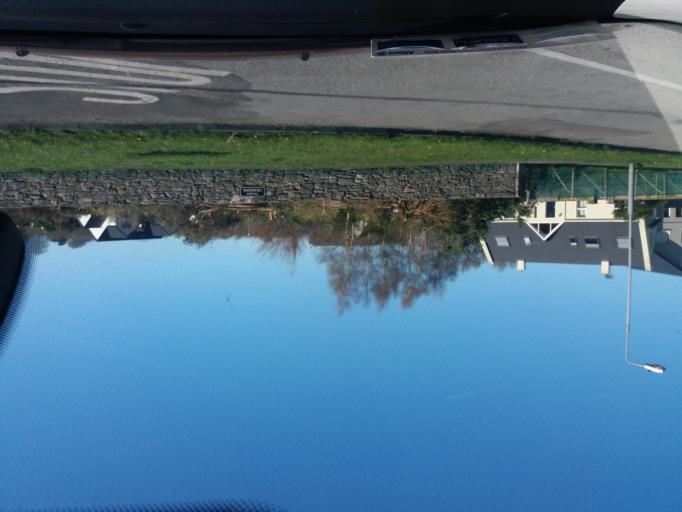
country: IE
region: Munster
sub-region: Ciarrai
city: Cill Airne
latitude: 52.0511
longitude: -9.5170
